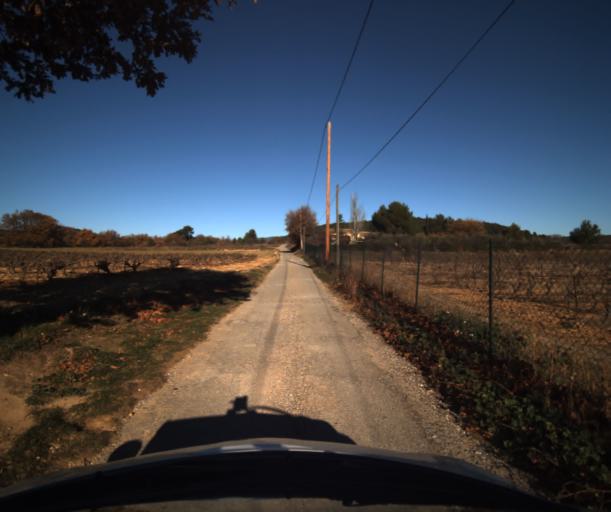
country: FR
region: Provence-Alpes-Cote d'Azur
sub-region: Departement du Vaucluse
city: Pertuis
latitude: 43.7081
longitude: 5.4994
